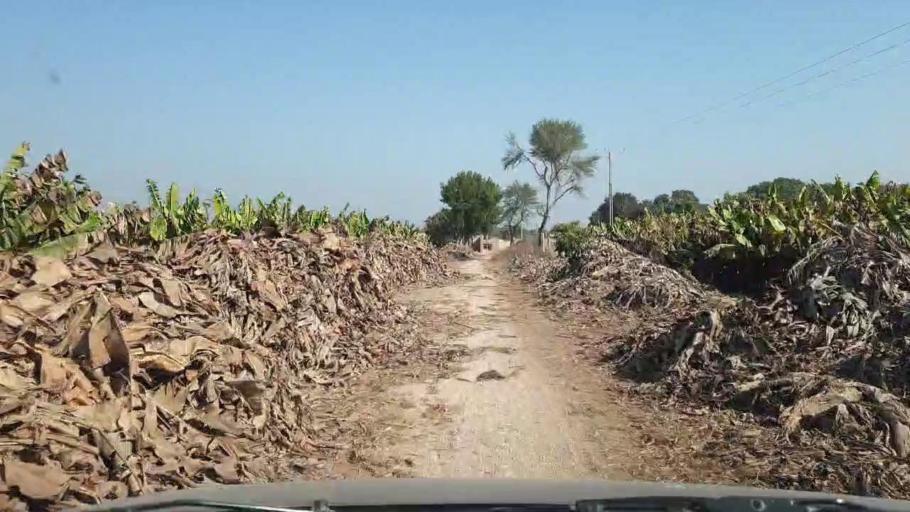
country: PK
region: Sindh
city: Tando Jam
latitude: 25.4427
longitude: 68.6119
